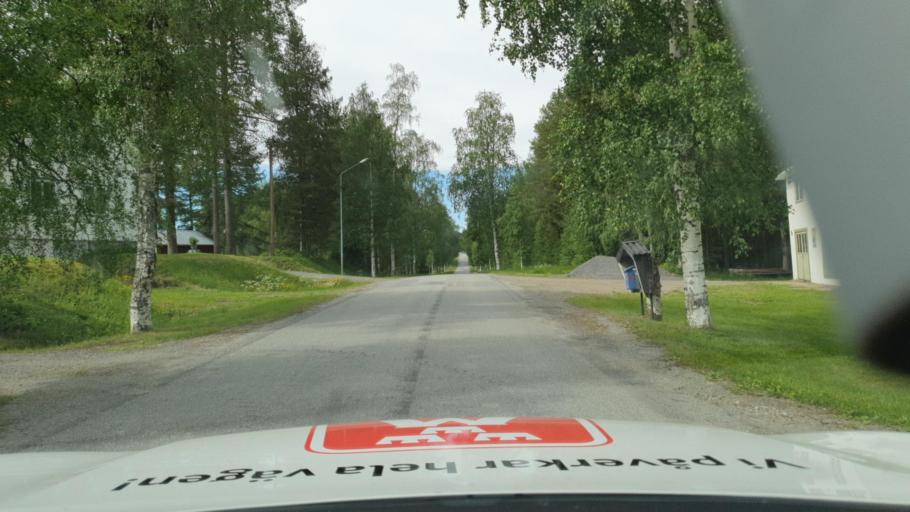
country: SE
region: Vaesterbotten
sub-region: Skelleftea Kommun
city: Burtraesk
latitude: 64.4304
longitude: 20.5207
